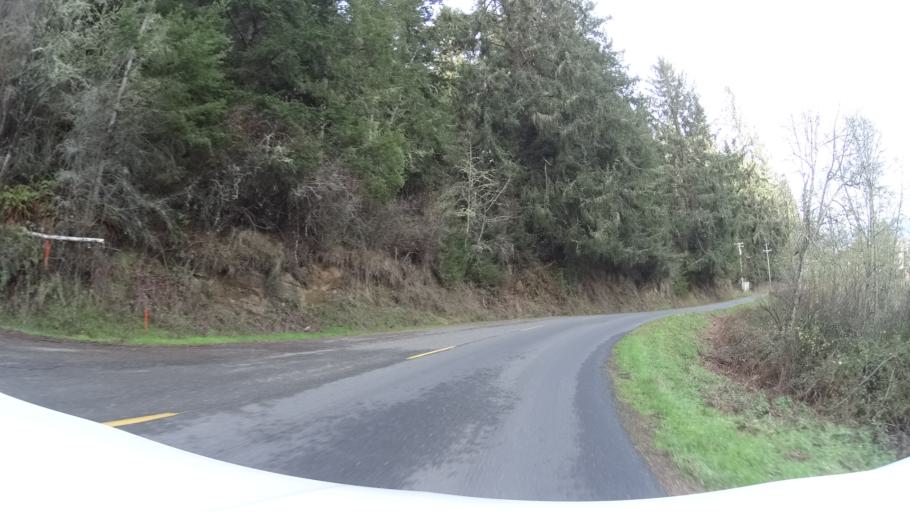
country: US
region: California
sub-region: Humboldt County
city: Ferndale
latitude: 40.5729
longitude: -124.2701
